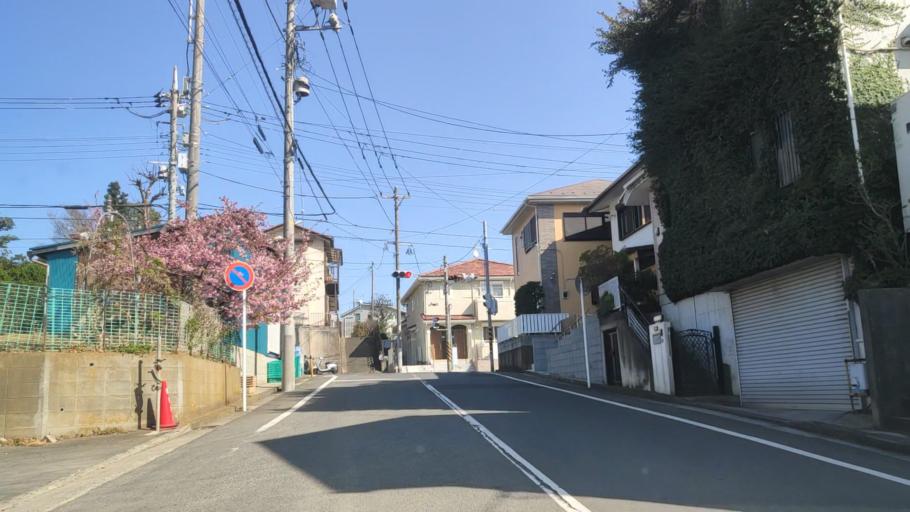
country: JP
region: Kanagawa
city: Yokohama
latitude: 35.5112
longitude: 139.6428
